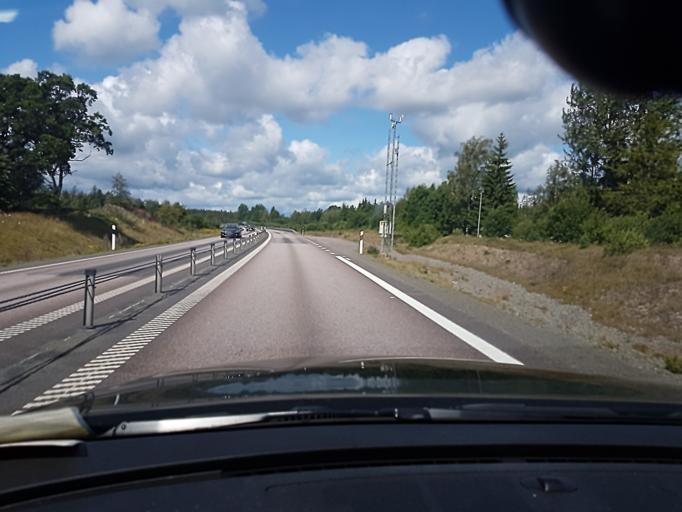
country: SE
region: Kalmar
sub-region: Emmaboda Kommun
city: Emmaboda
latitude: 56.7367
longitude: 15.5198
